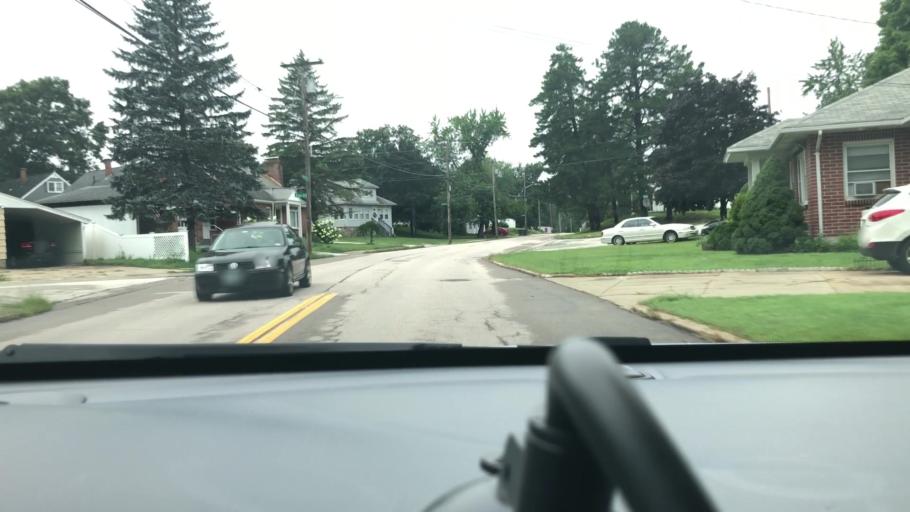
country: US
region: New Hampshire
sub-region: Hillsborough County
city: Pinardville
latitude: 42.9780
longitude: -71.4894
